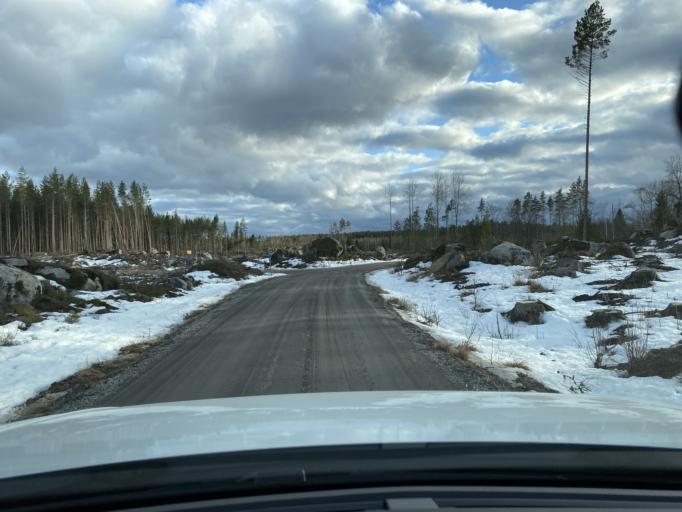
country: FI
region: Pirkanmaa
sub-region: Lounais-Pirkanmaa
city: Mouhijaervi
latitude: 61.4340
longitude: 22.9656
